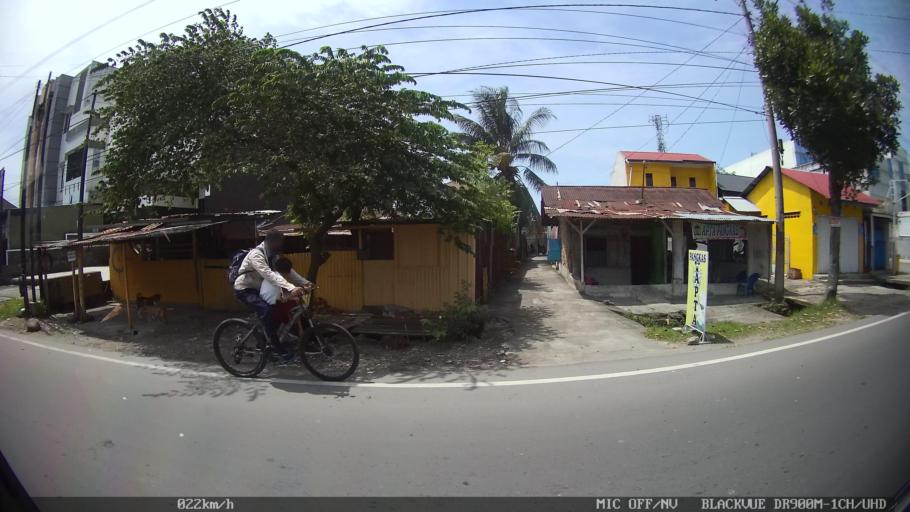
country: ID
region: North Sumatra
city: Sunggal
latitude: 3.5792
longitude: 98.6320
